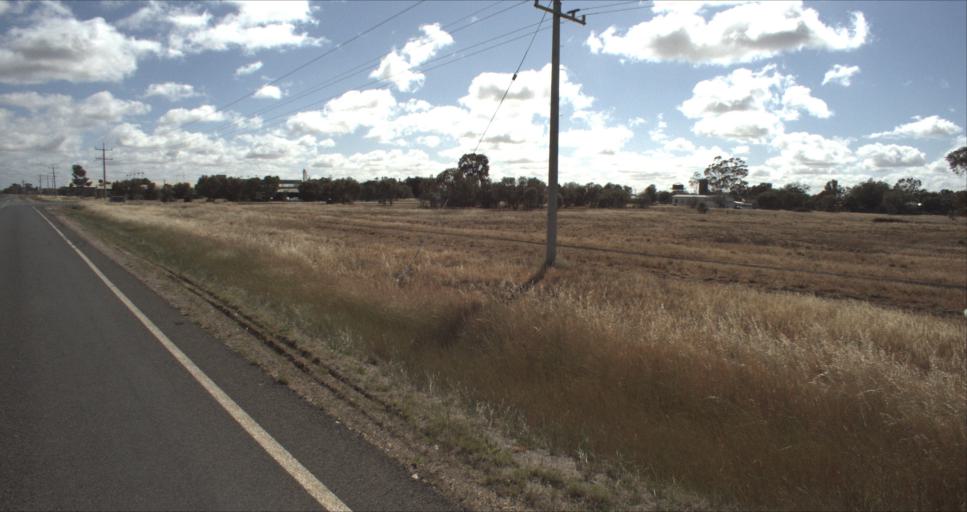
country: AU
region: New South Wales
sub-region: Murrumbidgee Shire
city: Darlington Point
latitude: -34.5183
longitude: 146.1762
